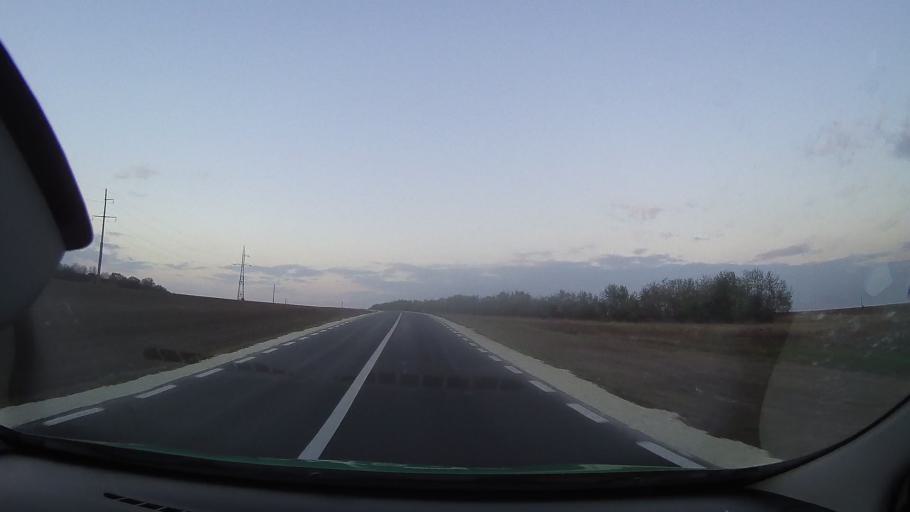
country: RO
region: Constanta
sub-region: Comuna Baneasa
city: Baneasa
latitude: 44.1073
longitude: 27.6709
